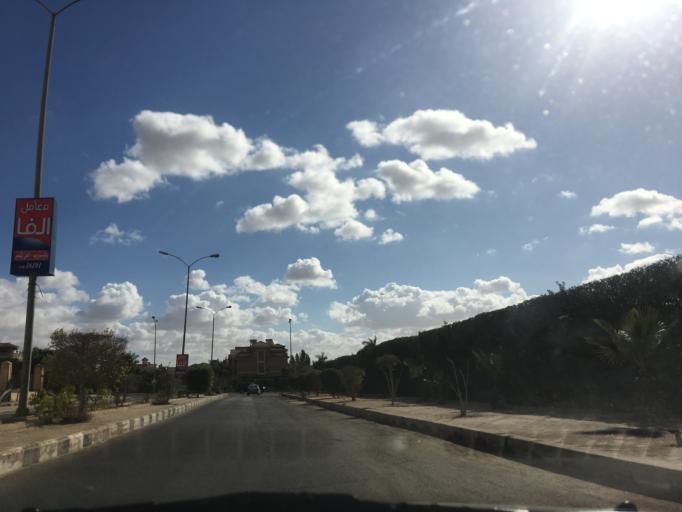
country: EG
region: Al Jizah
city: Madinat Sittah Uktubar
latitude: 29.9968
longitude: 30.9696
